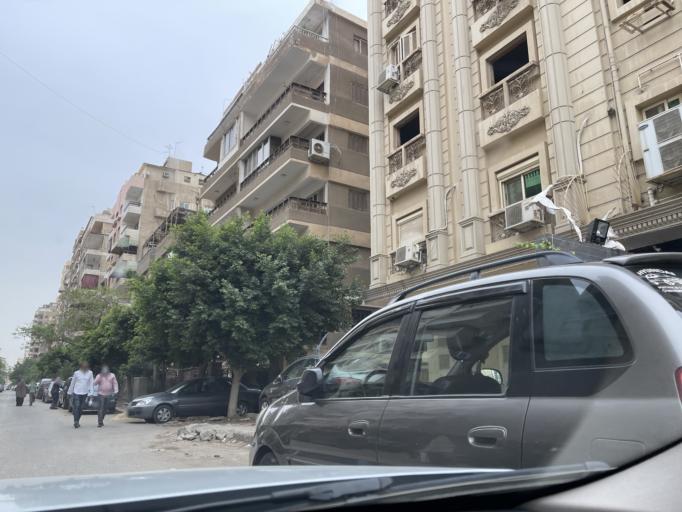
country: EG
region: Muhafazat al Qahirah
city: Cairo
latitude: 30.0590
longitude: 31.3473
